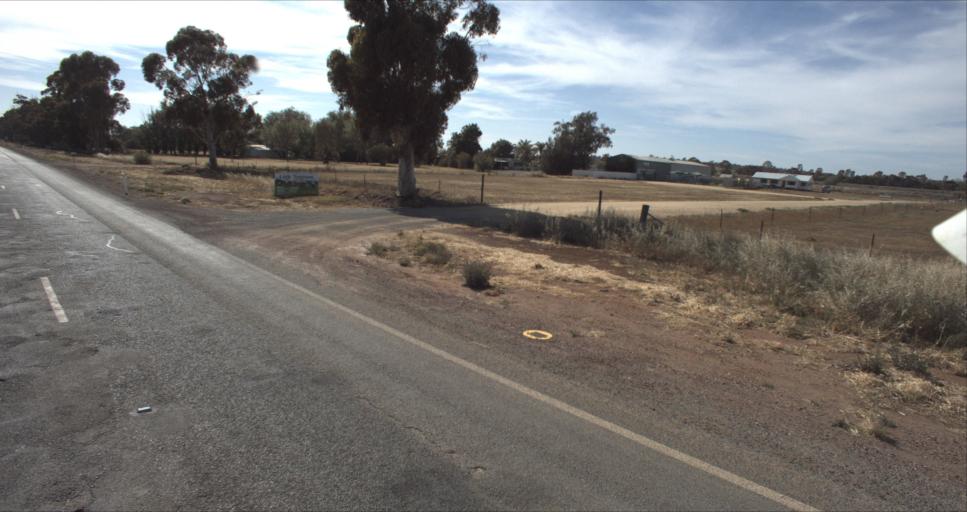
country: AU
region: New South Wales
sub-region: Leeton
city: Leeton
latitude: -34.5634
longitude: 146.4293
